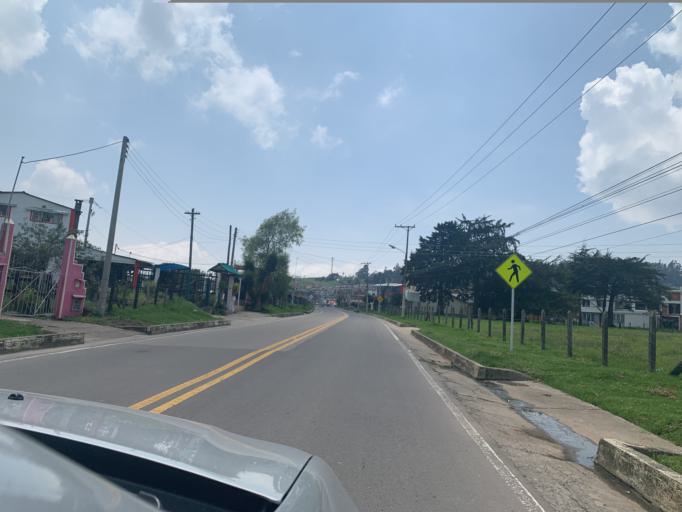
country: CO
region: Boyaca
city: Chiquinquira
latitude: 5.6245
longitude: -73.8051
